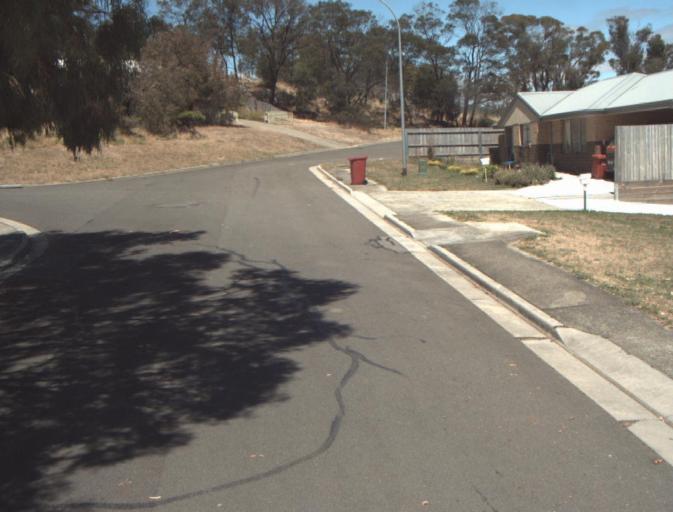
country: AU
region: Tasmania
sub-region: Launceston
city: Mayfield
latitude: -41.3786
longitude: 147.1379
